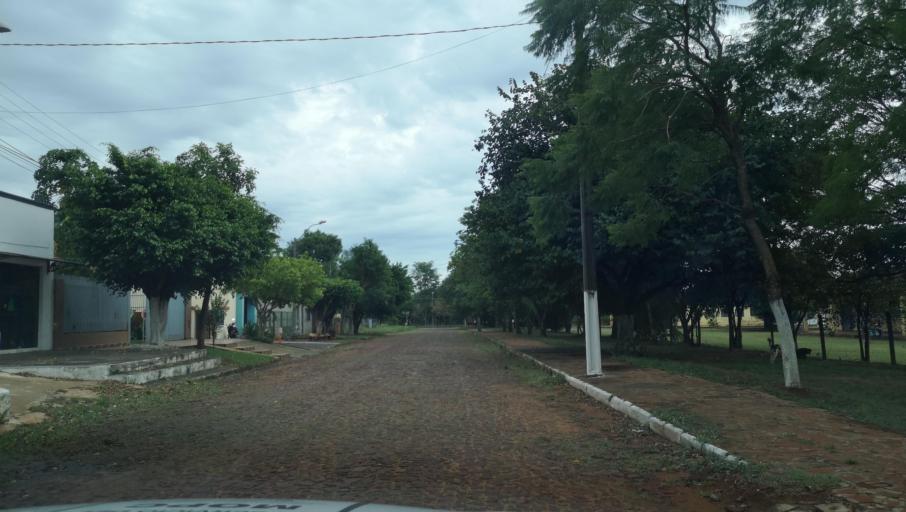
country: PY
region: Misiones
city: Santa Maria
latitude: -26.8865
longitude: -57.0369
